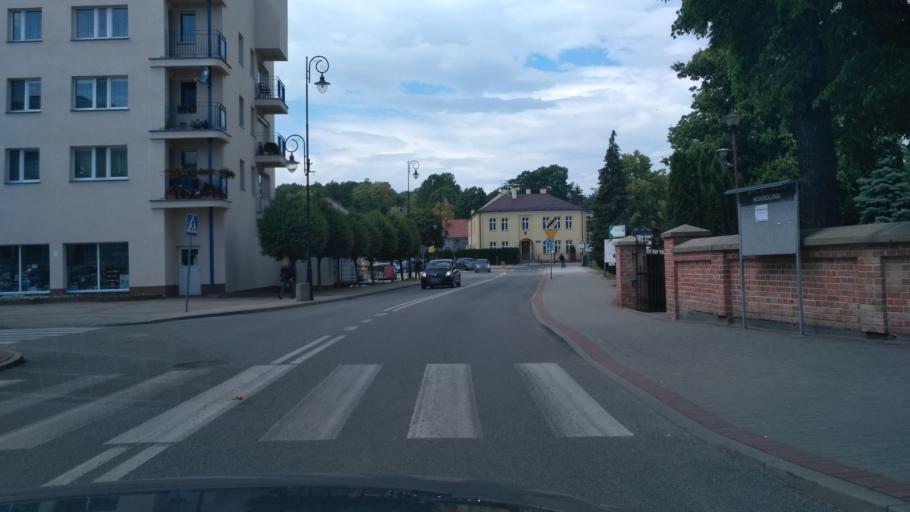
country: PL
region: Subcarpathian Voivodeship
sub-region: Powiat ropczycko-sedziszowski
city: Ropczyce
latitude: 50.0534
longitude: 21.6105
